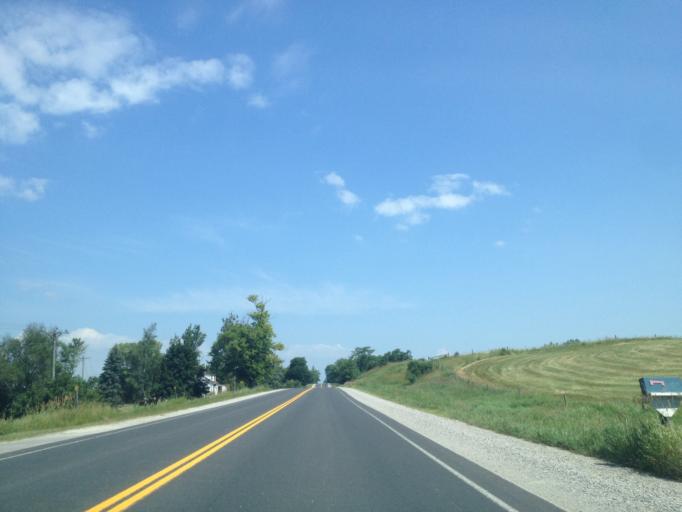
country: CA
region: Ontario
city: Stratford
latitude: 43.3091
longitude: -81.2008
